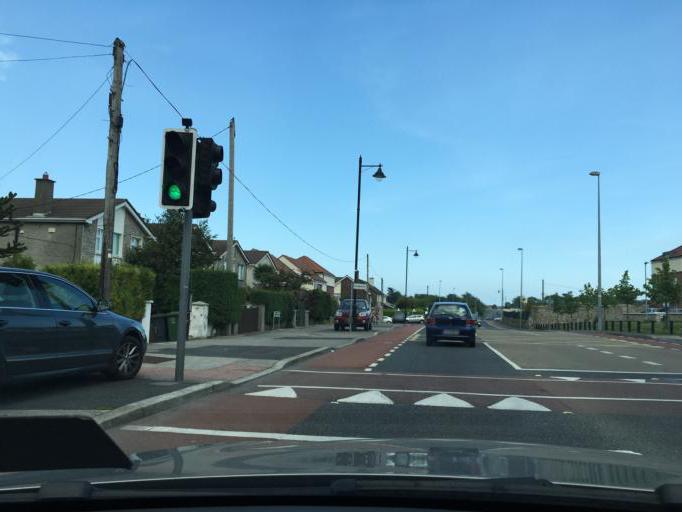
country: IE
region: Leinster
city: Templeogue
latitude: 53.2817
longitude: -6.2922
